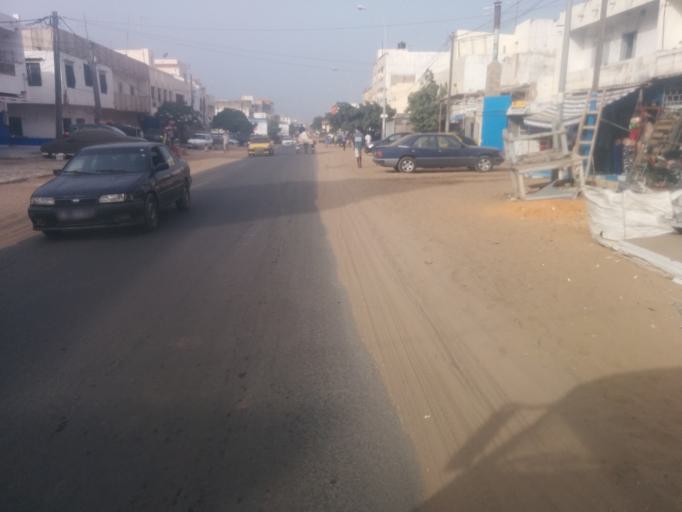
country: SN
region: Dakar
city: Grand Dakar
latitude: 14.7603
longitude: -17.4414
